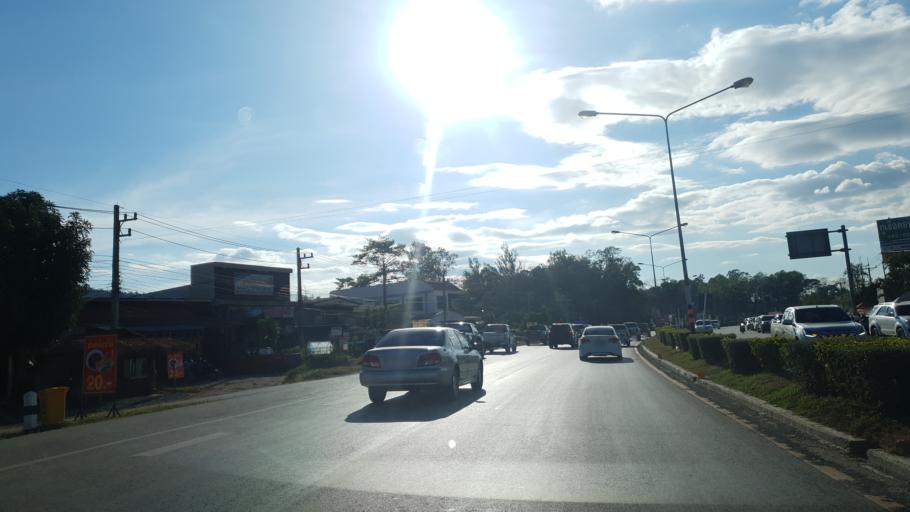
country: TH
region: Loei
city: Phu Ruea
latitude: 17.4501
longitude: 101.3588
